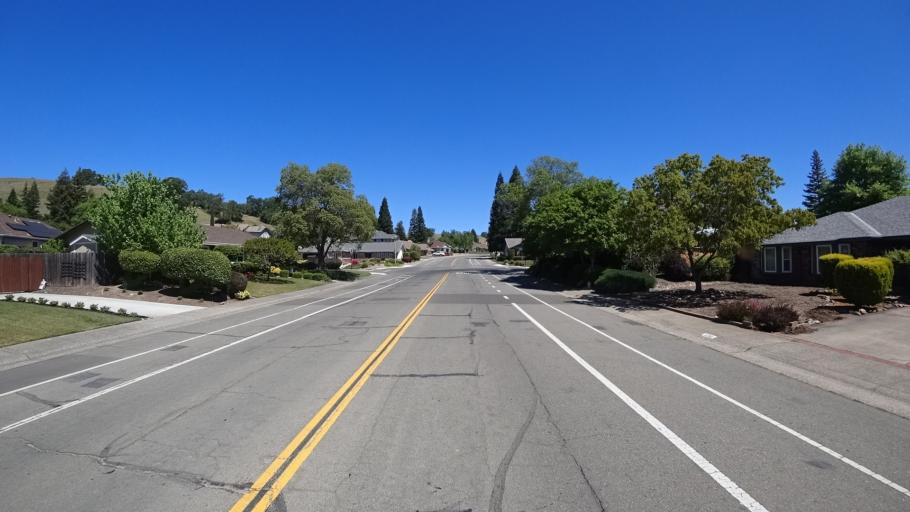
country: US
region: California
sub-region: Placer County
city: Rocklin
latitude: 38.8026
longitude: -121.2344
